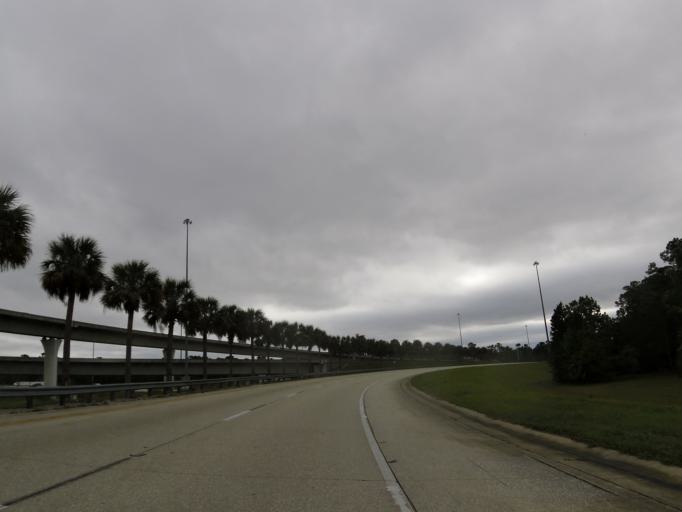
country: US
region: Florida
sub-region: Saint Johns County
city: Fruit Cove
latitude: 30.1694
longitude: -81.5585
